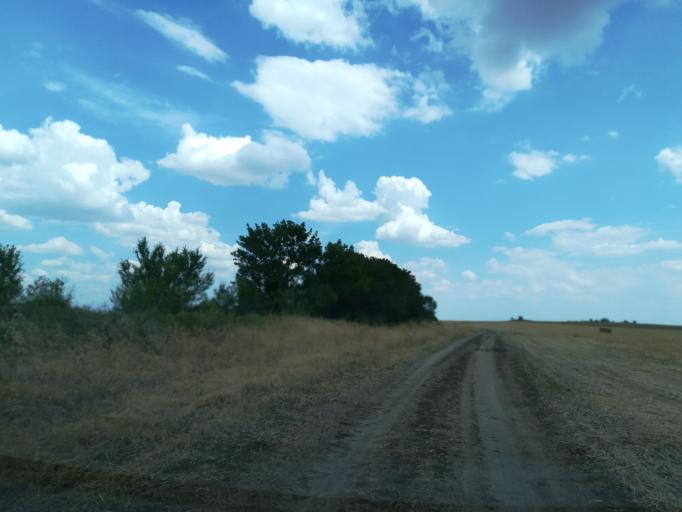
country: BG
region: Khaskovo
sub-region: Obshtina Mineralni Bani
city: Mineralni Bani
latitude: 42.0001
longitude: 25.1951
